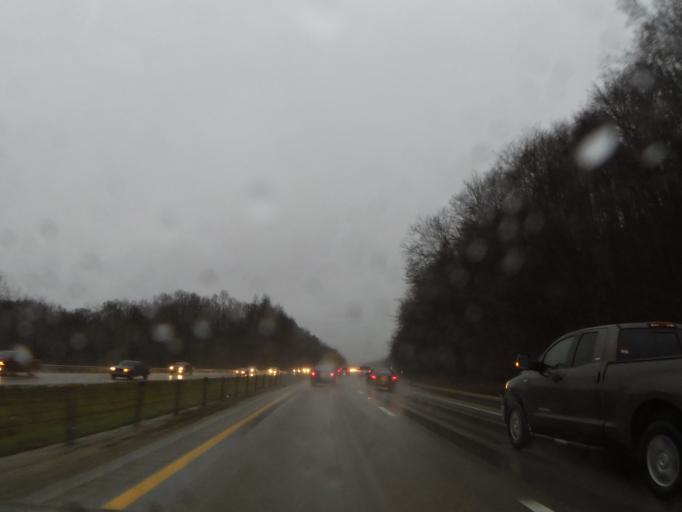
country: US
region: Kentucky
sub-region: Rockcastle County
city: Mount Vernon
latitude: 37.3186
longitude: -84.2937
